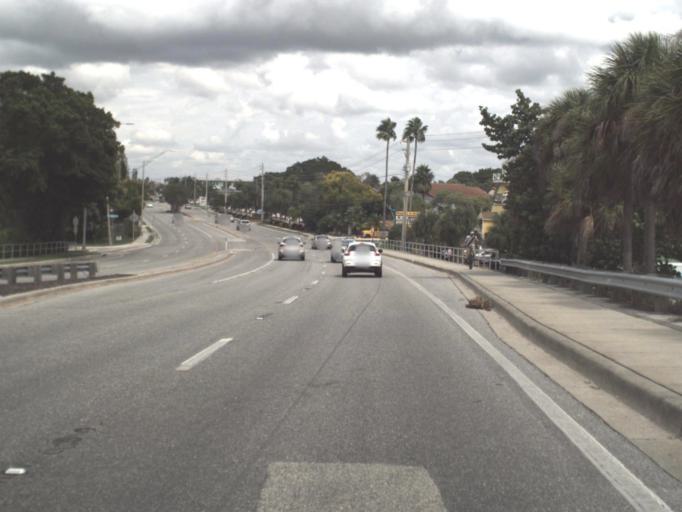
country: US
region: Florida
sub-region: Sarasota County
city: Gulf Gate Estates
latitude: 27.2546
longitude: -82.5308
